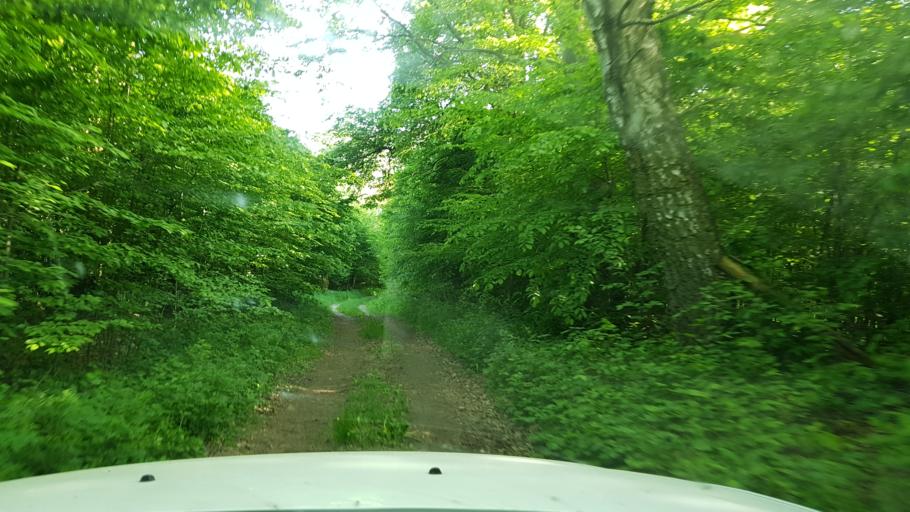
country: PL
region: West Pomeranian Voivodeship
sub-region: Powiat lobeski
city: Dobra
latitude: 53.6896
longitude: 15.3359
